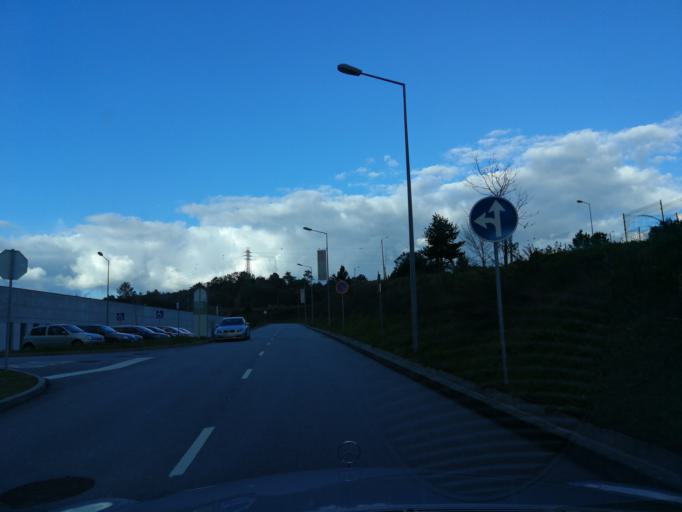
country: PT
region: Braga
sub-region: Braga
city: Adaufe
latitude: 41.5669
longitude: -8.3982
